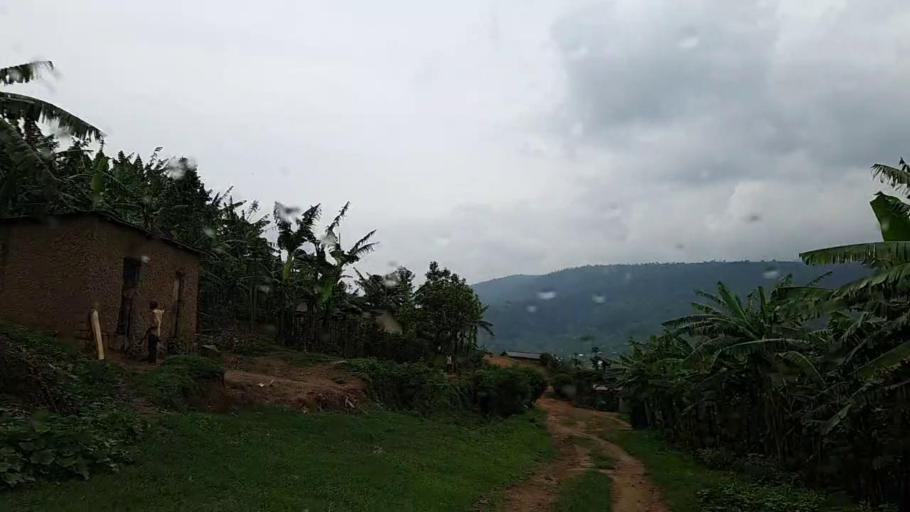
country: RW
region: Kigali
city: Kigali
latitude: -1.9027
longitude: 29.9550
